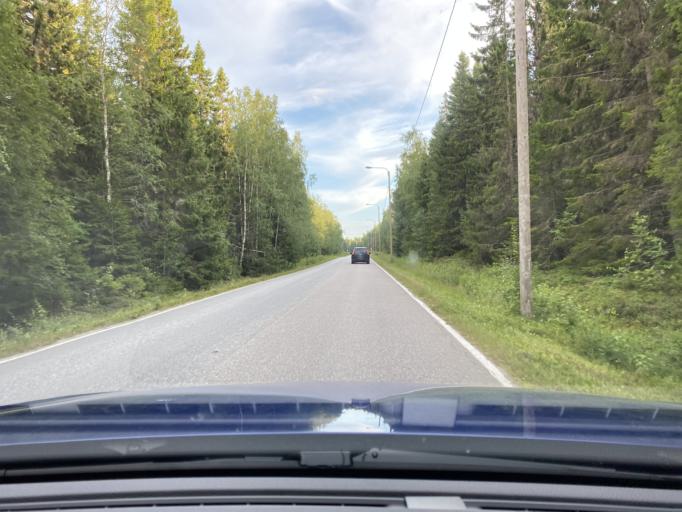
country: FI
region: Ostrobothnia
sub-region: Vaasa
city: Korsnaes
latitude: 62.9492
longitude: 21.1760
